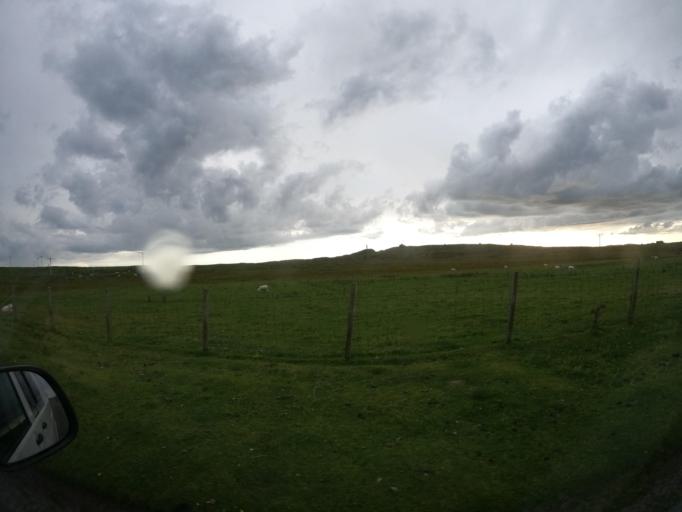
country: GB
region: Scotland
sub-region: Eilean Siar
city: Barra
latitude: 56.5117
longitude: -6.8139
